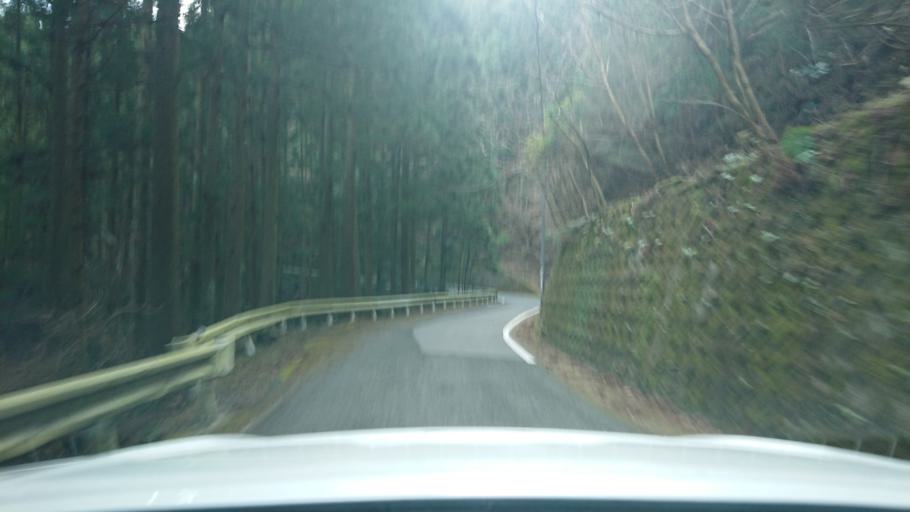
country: JP
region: Tokushima
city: Ishii
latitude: 33.9134
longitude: 134.3983
